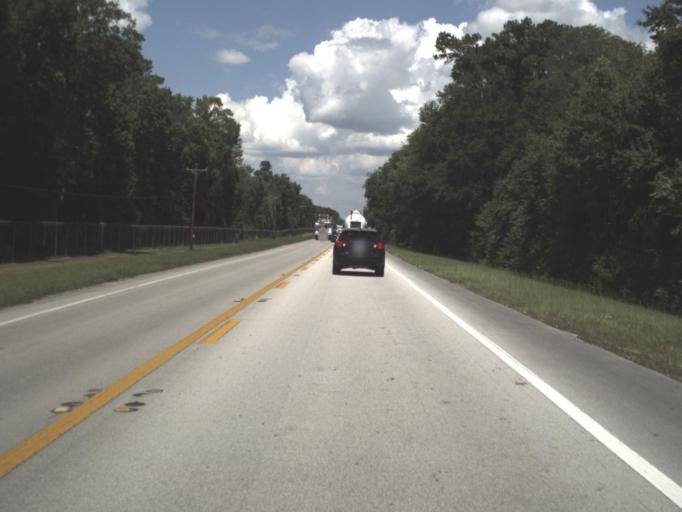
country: US
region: Florida
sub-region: Clay County
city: Keystone Heights
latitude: 29.7070
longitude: -82.0767
